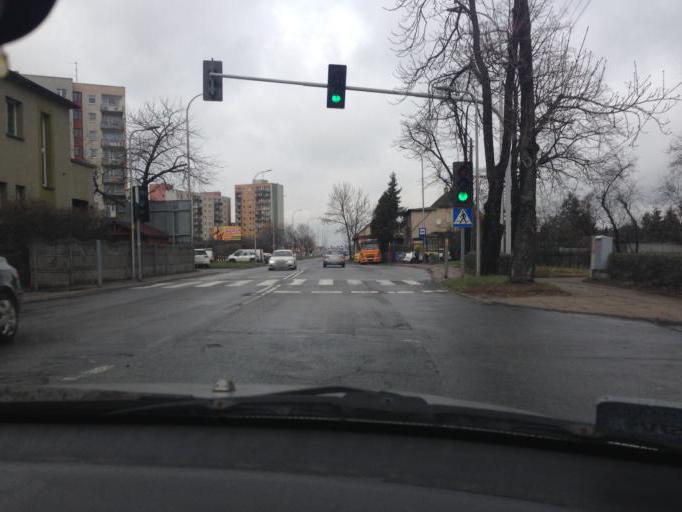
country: PL
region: Opole Voivodeship
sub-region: Powiat opolski
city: Opole
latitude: 50.6827
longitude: 17.9547
